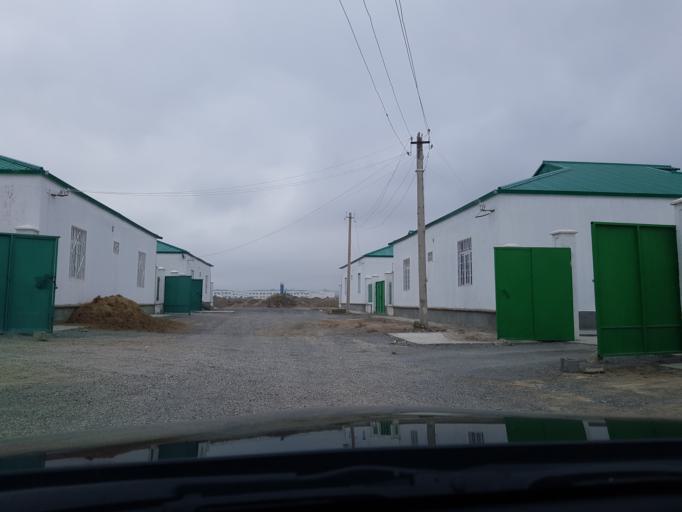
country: TM
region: Ahal
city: Abadan
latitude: 38.1580
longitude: 57.9479
